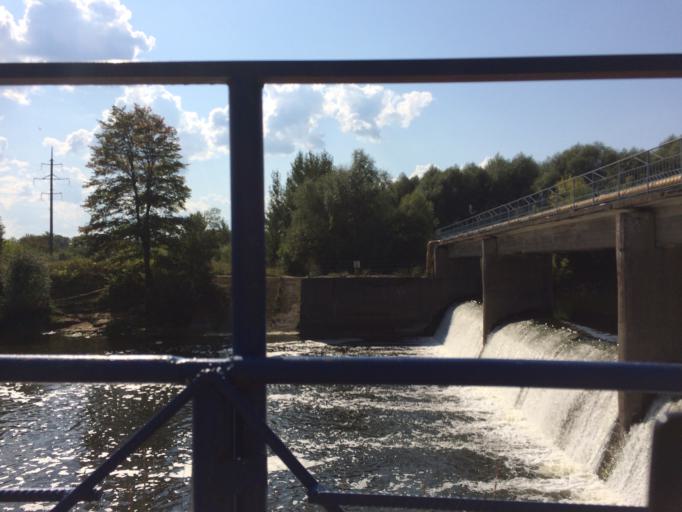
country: RU
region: Mariy-El
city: Yoshkar-Ola
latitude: 56.6133
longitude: 47.9317
